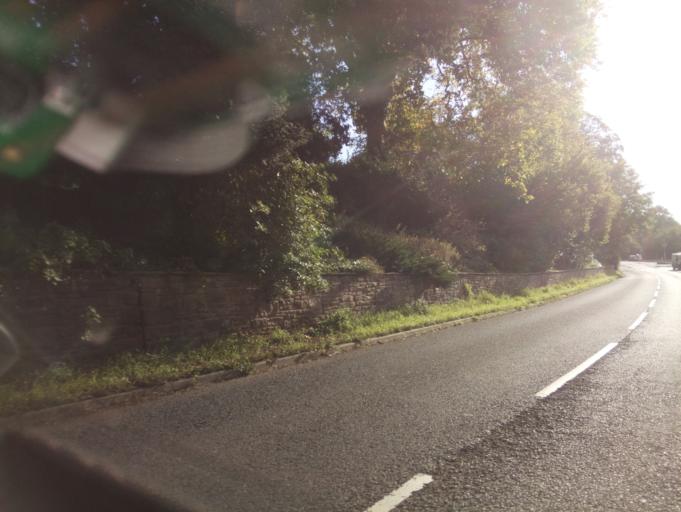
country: GB
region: Wales
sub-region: Sir Powys
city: Hay
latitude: 52.0459
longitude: -3.1949
